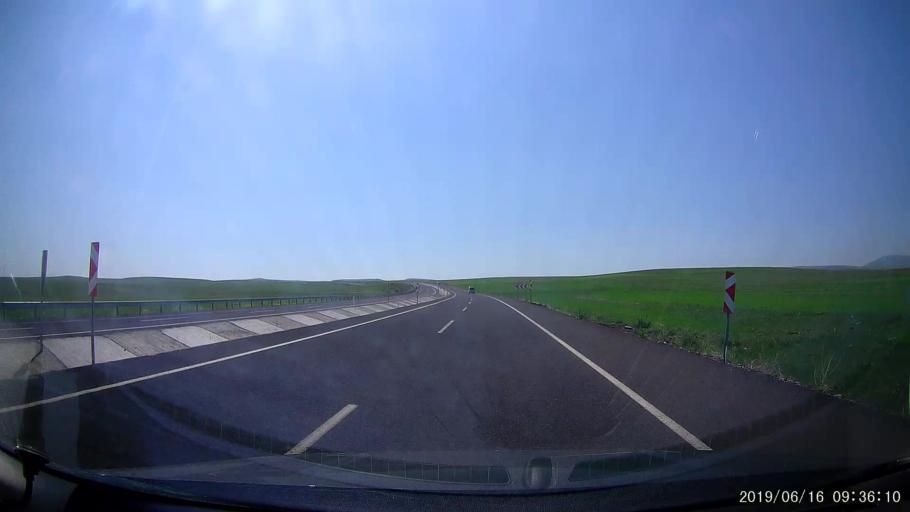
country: TR
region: Kars
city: Kars
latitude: 40.5608
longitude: 43.1676
